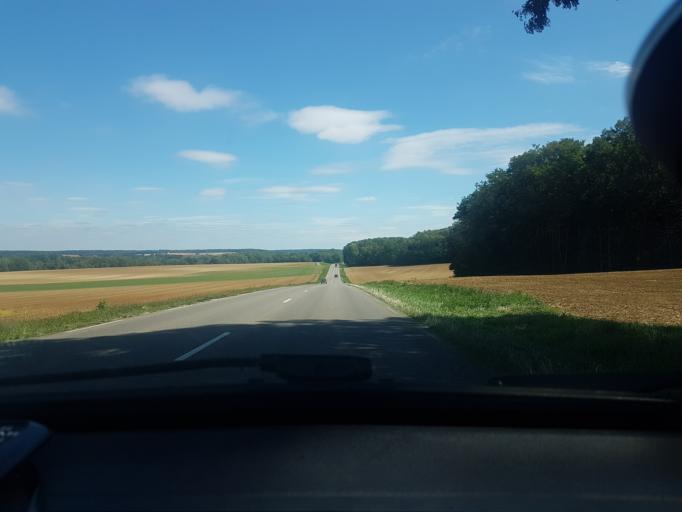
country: FR
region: Bourgogne
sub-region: Departement de la Cote-d'Or
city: Mirebeau-sur-Beze
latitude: 47.4054
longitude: 5.3597
